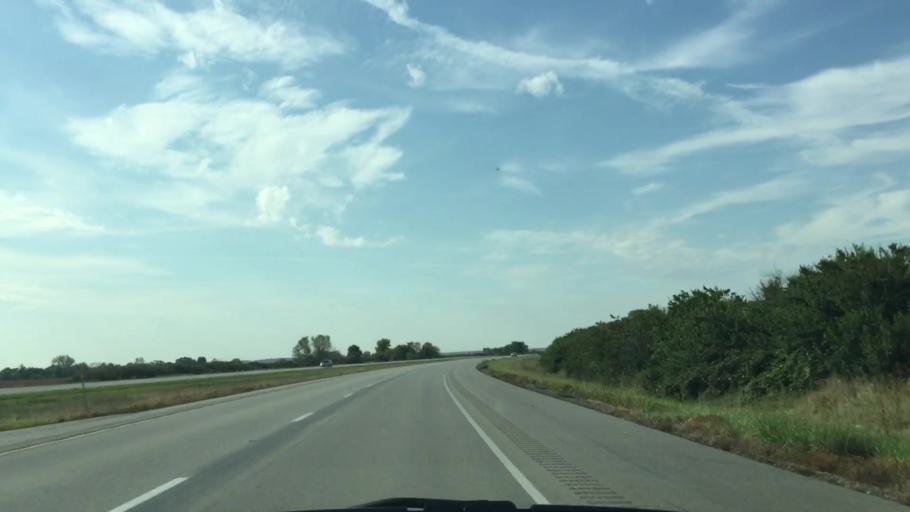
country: US
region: Illinois
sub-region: Whiteside County
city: Erie
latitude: 41.5960
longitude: -90.1936
